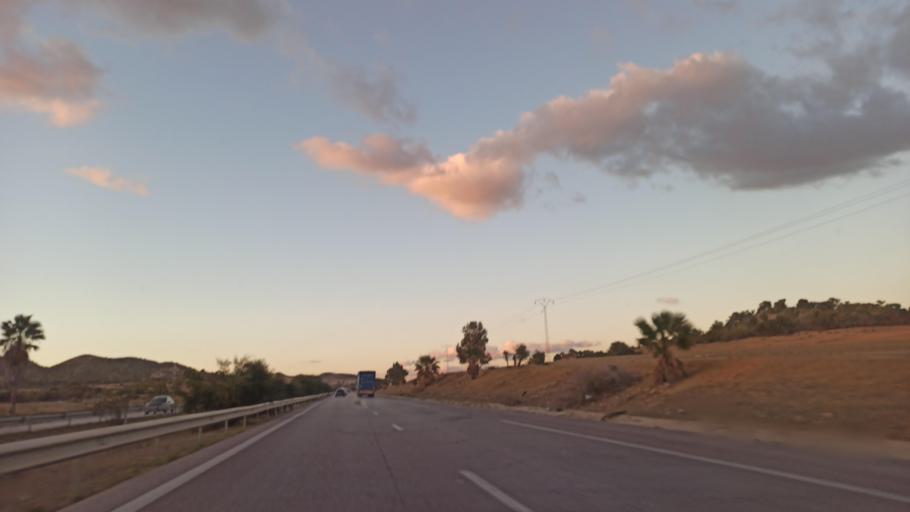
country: TN
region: Susah
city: Harqalah
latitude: 36.2200
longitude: 10.4183
